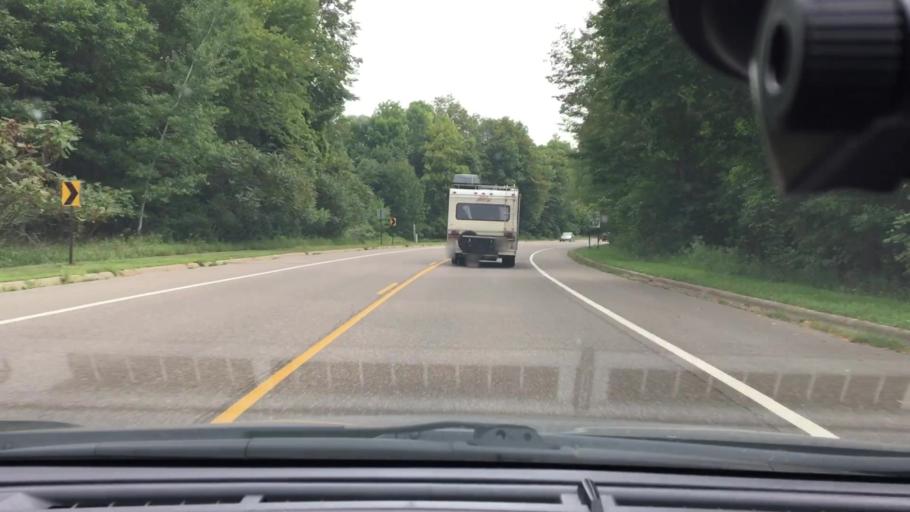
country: US
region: Minnesota
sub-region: Crow Wing County
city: Crosby
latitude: 46.4100
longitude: -93.8660
